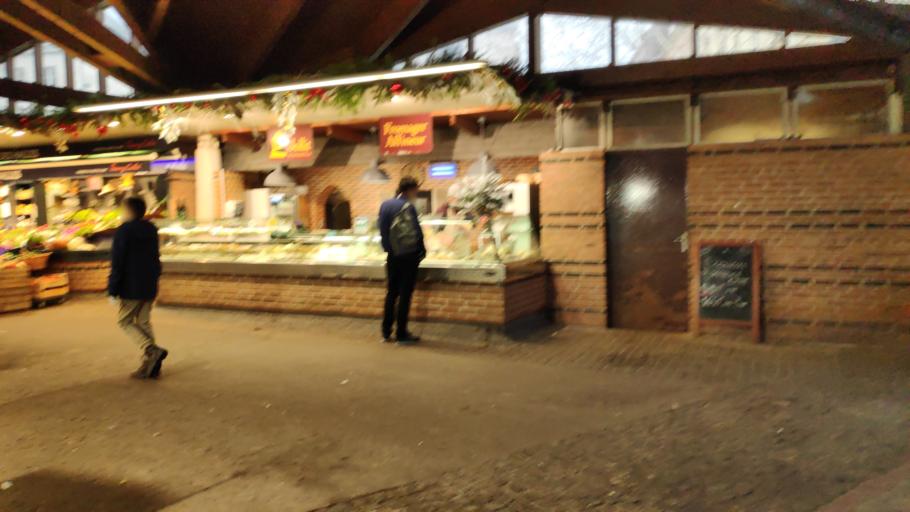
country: FR
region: Haute-Normandie
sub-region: Departement de la Seine-Maritime
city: Rouen
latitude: 49.4431
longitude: 1.0886
